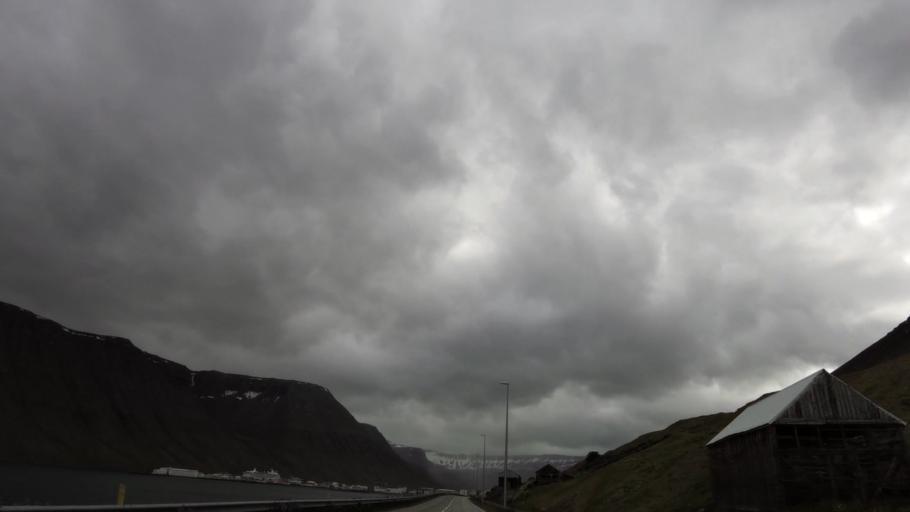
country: IS
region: Westfjords
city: Isafjoerdur
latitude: 66.0863
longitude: -23.1193
